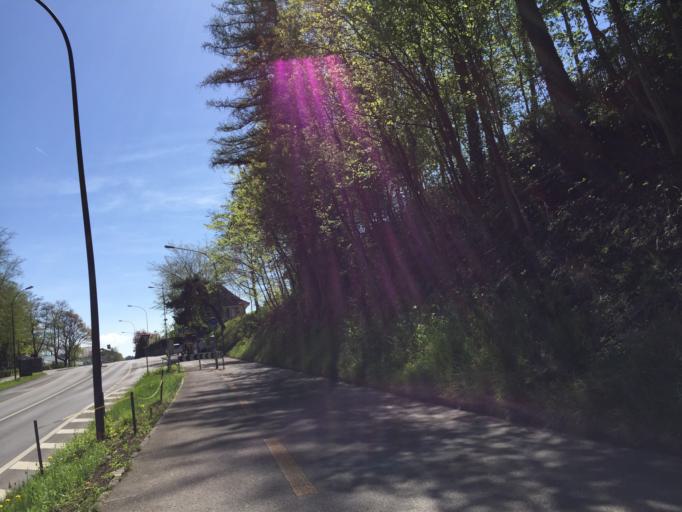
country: CH
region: Bern
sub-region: Bern-Mittelland District
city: Koniz
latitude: 46.9371
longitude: 7.4259
